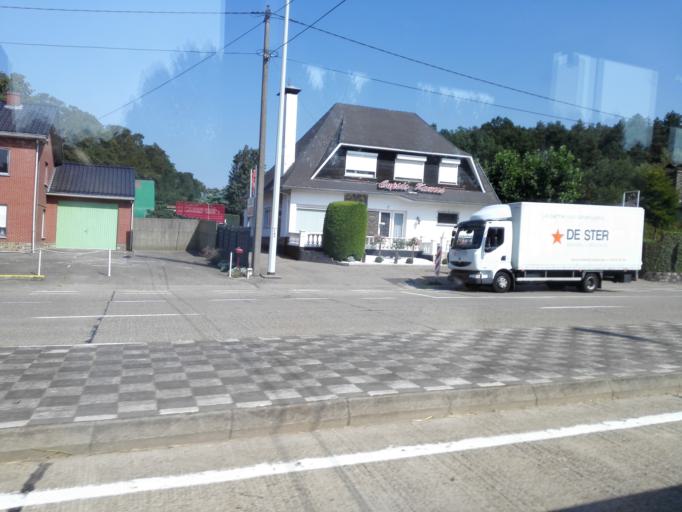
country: BE
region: Flanders
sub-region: Provincie Vlaams-Brabant
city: Bekkevoort
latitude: 50.9536
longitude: 5.0022
